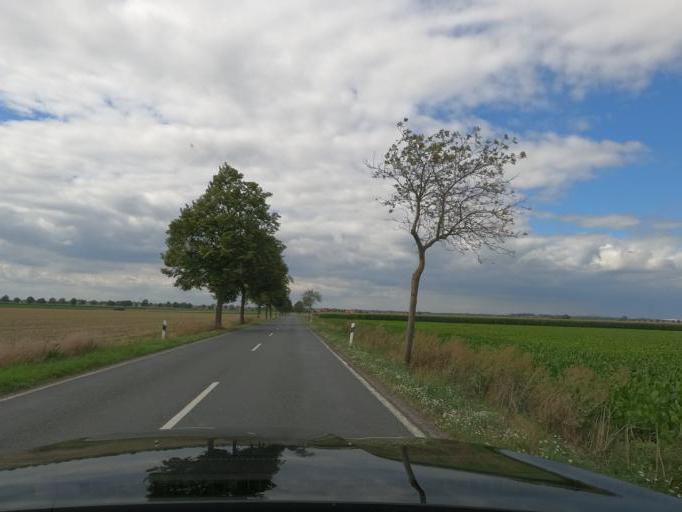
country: DE
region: Lower Saxony
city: Algermissen
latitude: 52.2460
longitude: 9.9980
